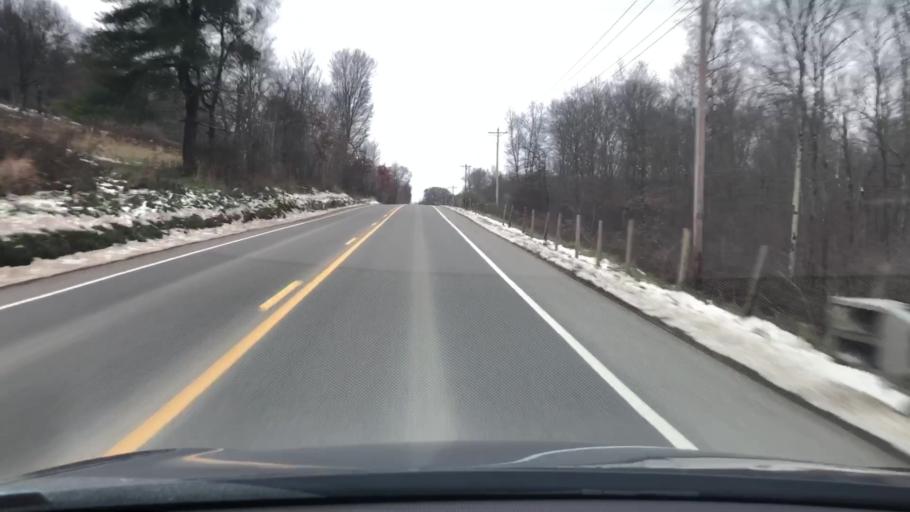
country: US
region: Pennsylvania
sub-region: Jefferson County
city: Brookville
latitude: 41.0598
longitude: -79.2465
